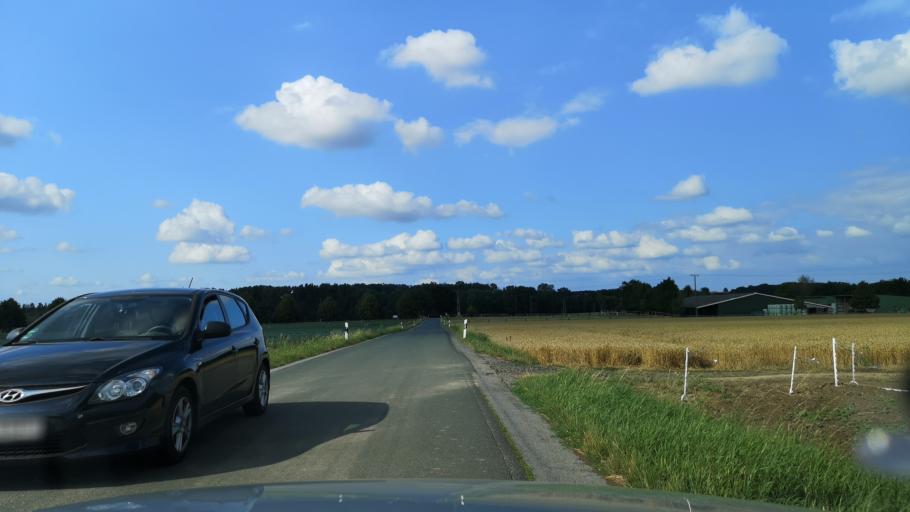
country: DE
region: North Rhine-Westphalia
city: Iserlohn
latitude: 51.4346
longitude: 7.7094
